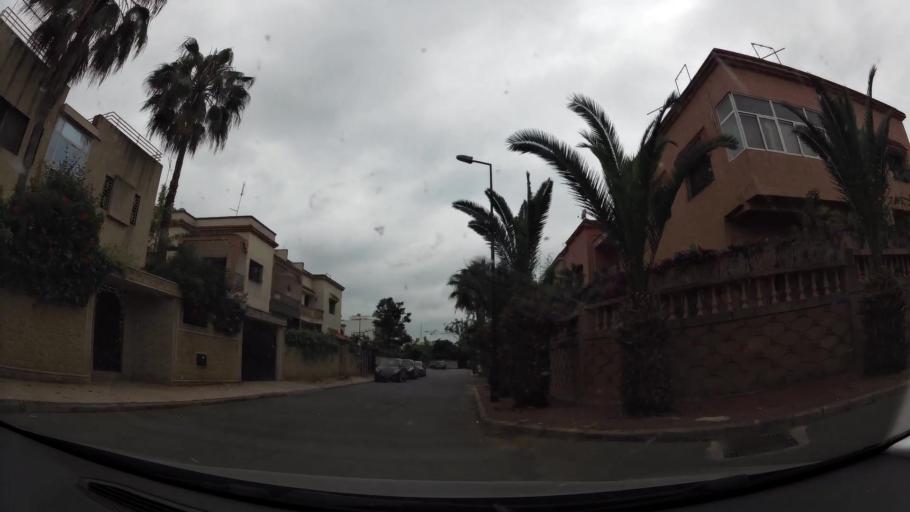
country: MA
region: Rabat-Sale-Zemmour-Zaer
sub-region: Rabat
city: Rabat
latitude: 33.9787
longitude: -6.8127
